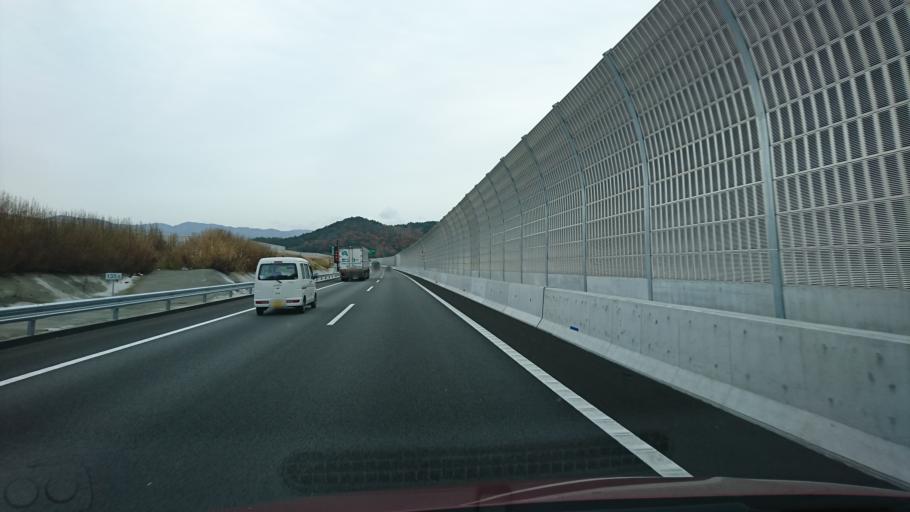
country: JP
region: Hyogo
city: Kawanishi
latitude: 34.8890
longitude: 135.3637
